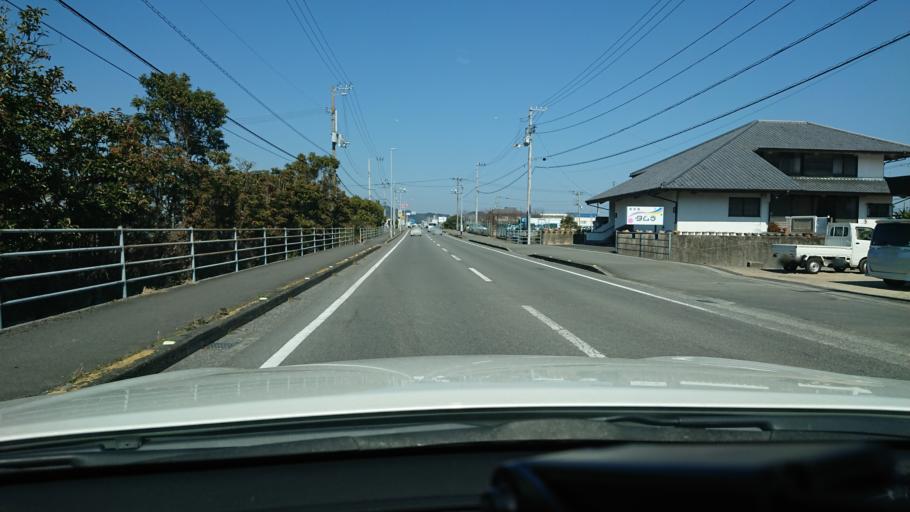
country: JP
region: Tokushima
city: Narutocho-mitsuishi
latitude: 34.1481
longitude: 134.5933
